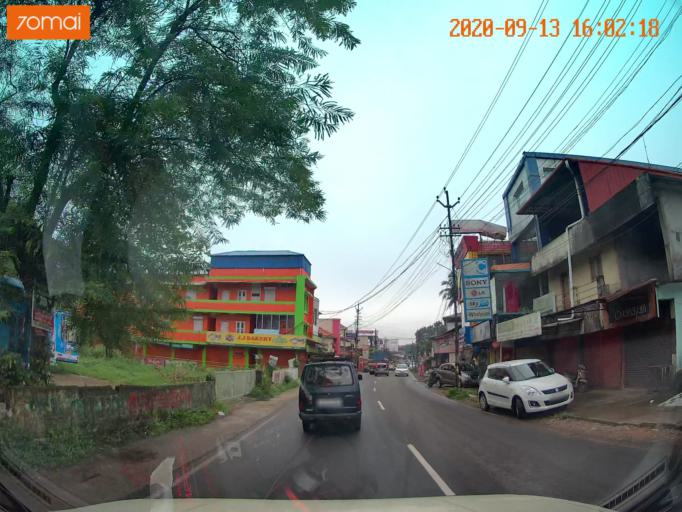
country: IN
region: Kerala
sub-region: Kottayam
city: Kottayam
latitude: 9.6711
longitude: 76.5604
